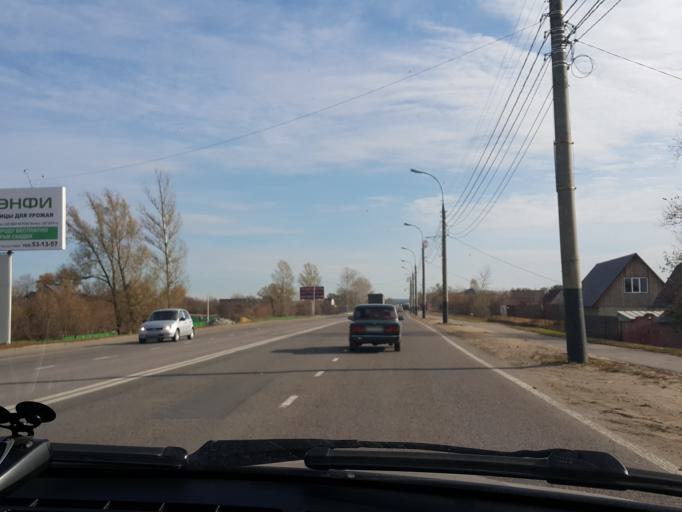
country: RU
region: Tambov
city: Tambov
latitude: 52.7238
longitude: 41.4725
